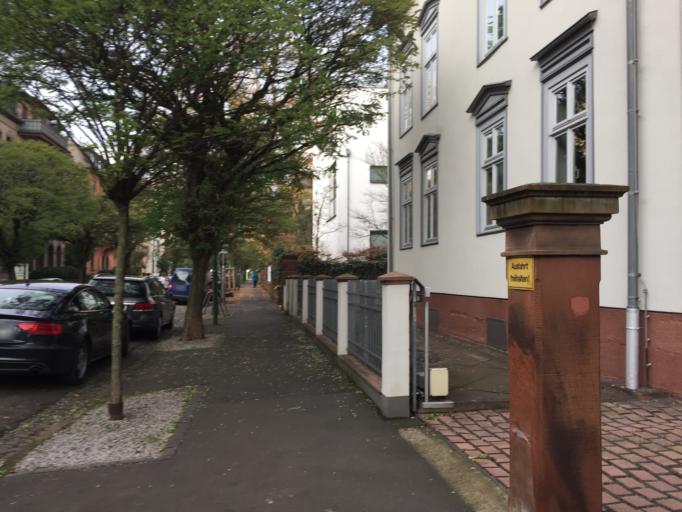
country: DE
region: Hesse
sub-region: Regierungsbezirk Giessen
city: Marburg an der Lahn
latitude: 50.8030
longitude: 8.7665
